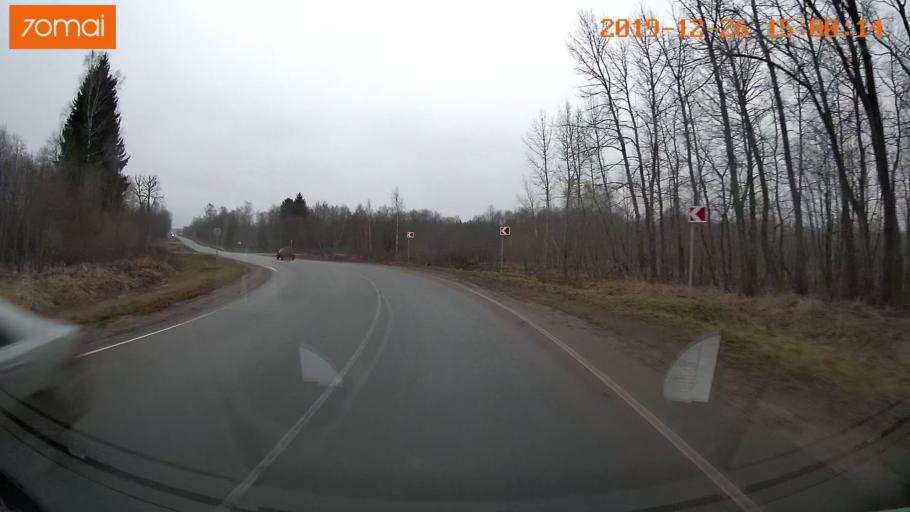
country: RU
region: Jaroslavl
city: Rybinsk
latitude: 58.2482
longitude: 38.8495
